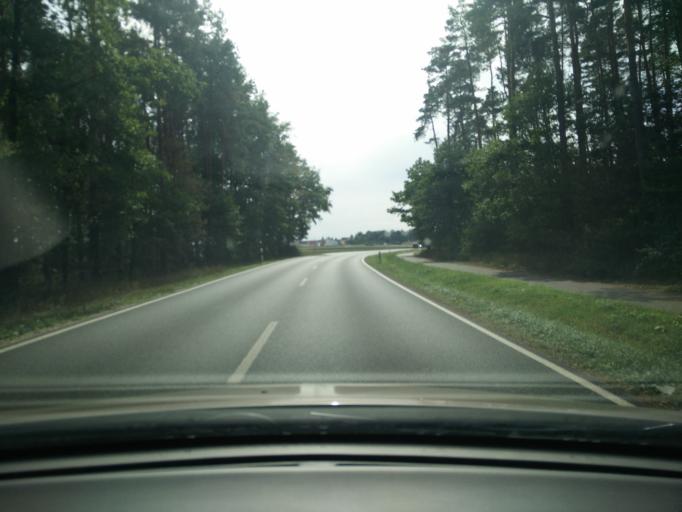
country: DE
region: Bavaria
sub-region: Regierungsbezirk Mittelfranken
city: Seukendorf
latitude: 49.4989
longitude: 10.8791
